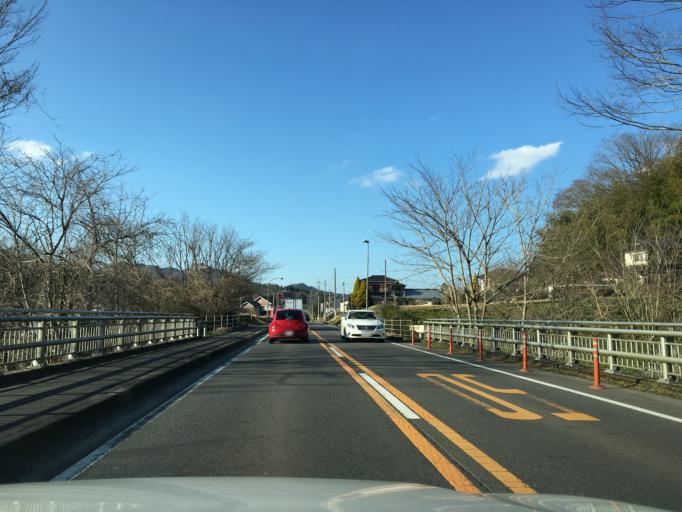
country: JP
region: Ibaraki
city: Daigo
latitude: 36.7023
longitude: 140.3835
